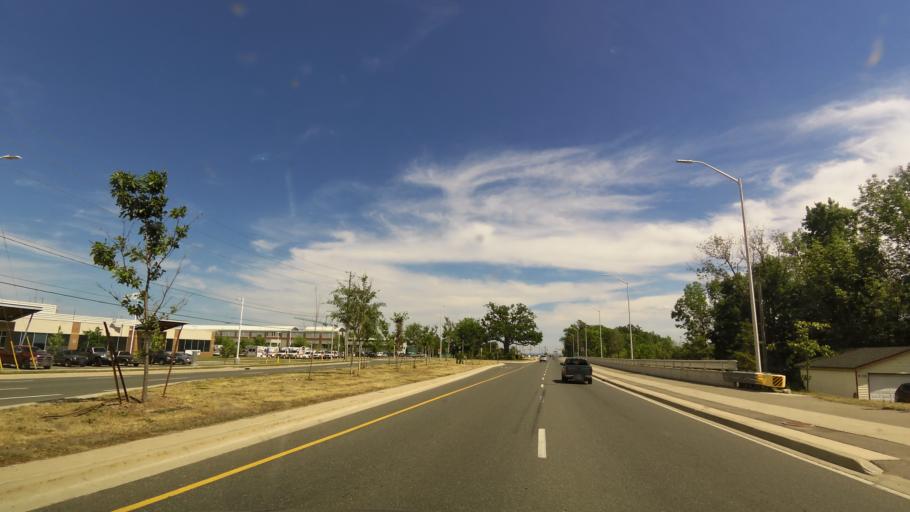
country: CA
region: Ontario
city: Oakville
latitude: 43.4151
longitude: -79.7478
